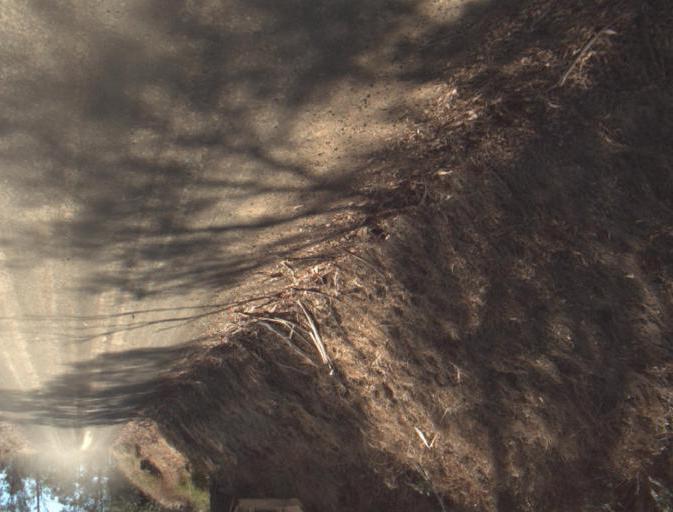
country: AU
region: Tasmania
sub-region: Launceston
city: Mayfield
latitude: -41.2487
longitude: 147.1346
